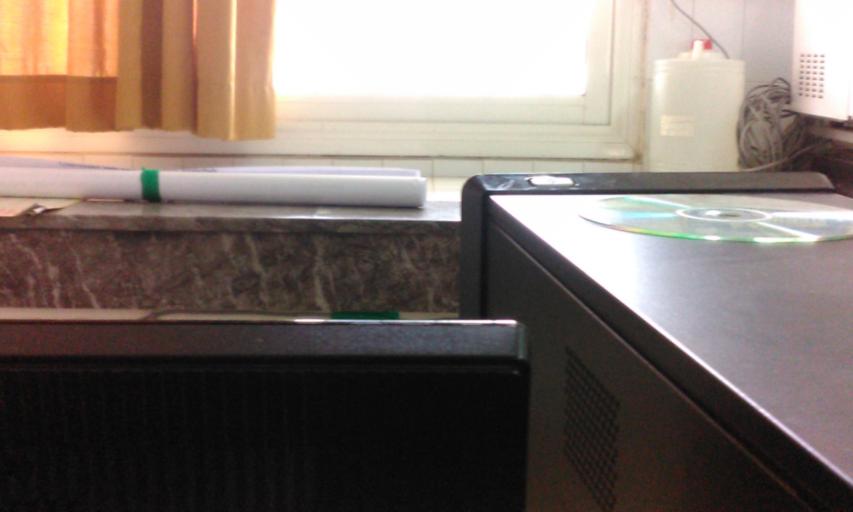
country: MA
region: Fes-Boulemane
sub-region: Fes
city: Oulad Tayeb
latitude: 33.9904
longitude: -4.9889
